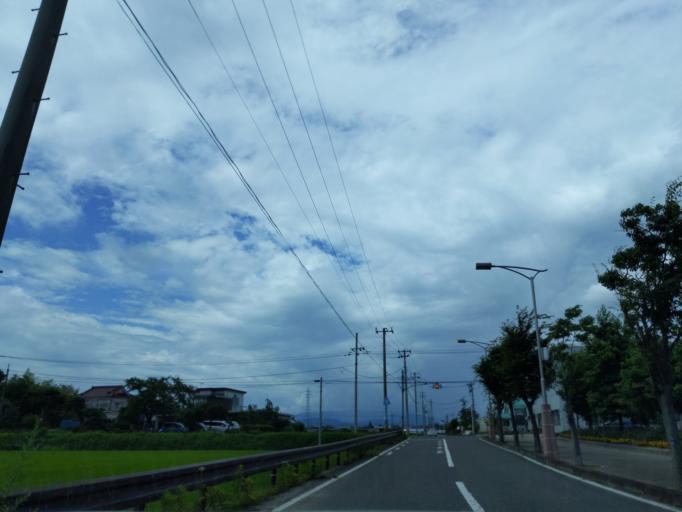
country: JP
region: Fukushima
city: Koriyama
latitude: 37.3645
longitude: 140.3525
